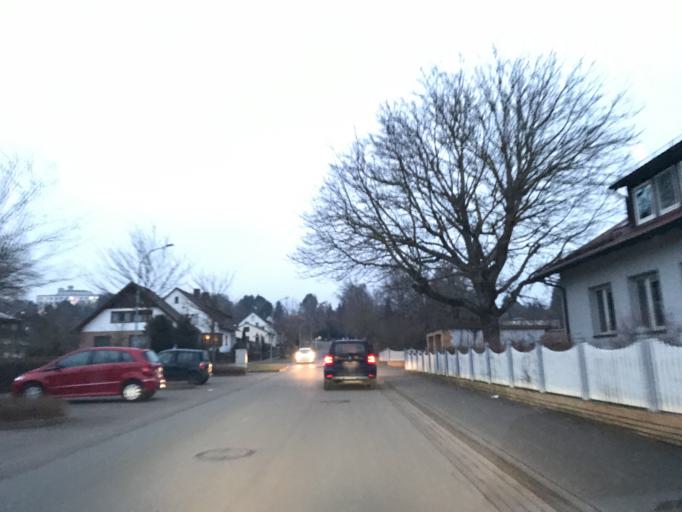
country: DE
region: Hesse
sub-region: Regierungsbezirk Kassel
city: Hofgeismar
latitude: 51.4927
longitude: 9.3738
